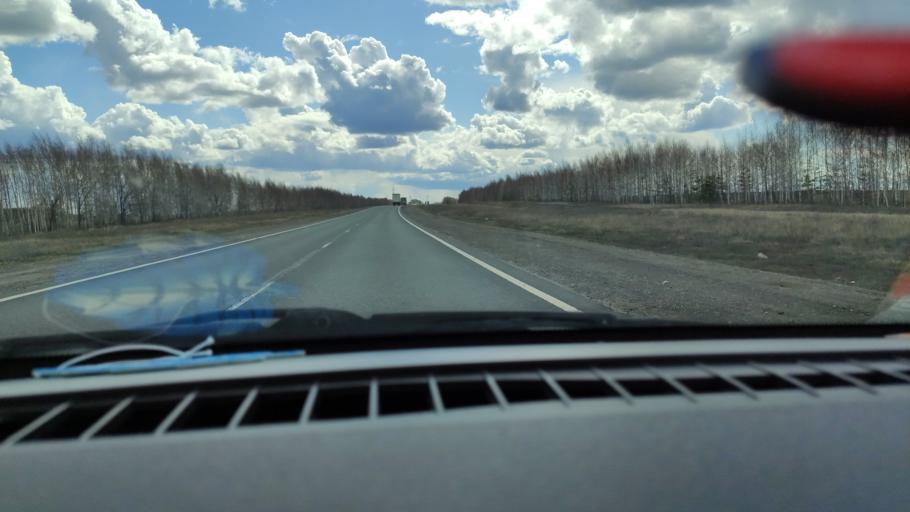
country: RU
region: Saratov
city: Dukhovnitskoye
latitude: 52.8448
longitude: 48.2513
